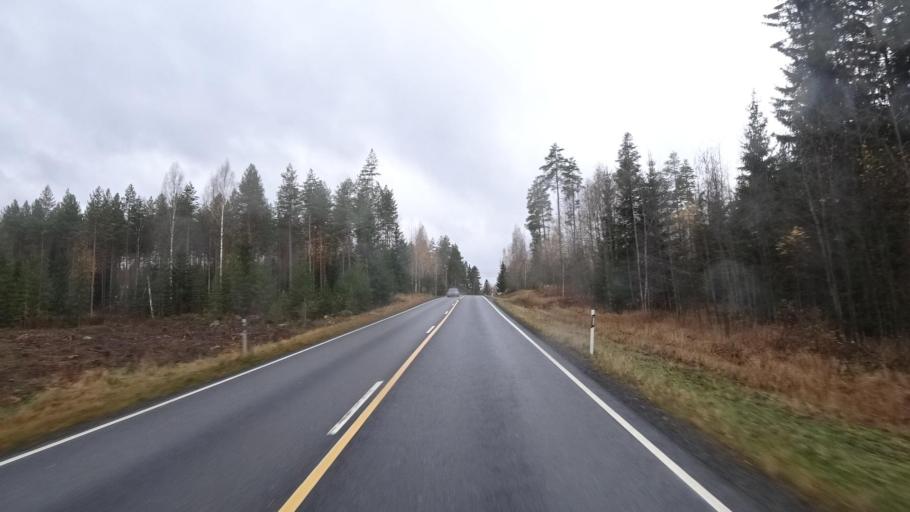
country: FI
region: Southern Savonia
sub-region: Mikkeli
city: Kangasniemi
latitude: 62.1680
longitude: 26.8488
